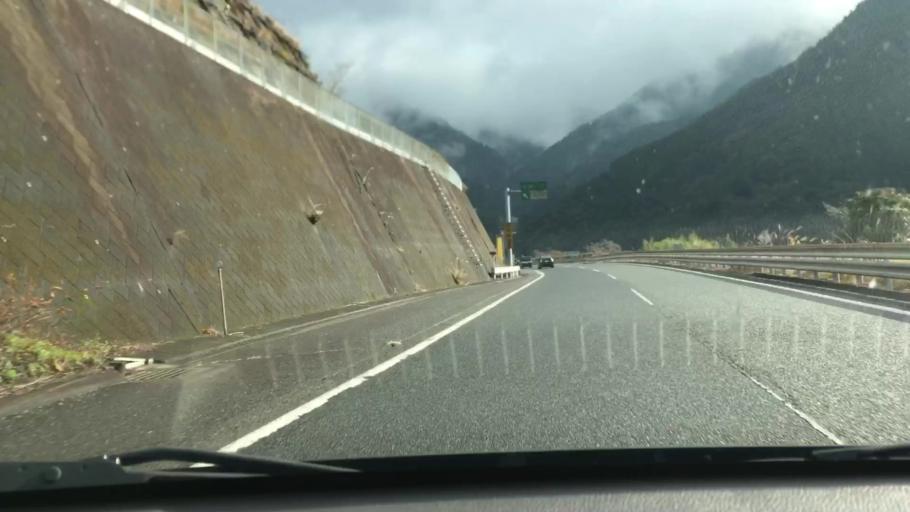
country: JP
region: Kumamoto
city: Yatsushiro
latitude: 32.3986
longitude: 130.7026
